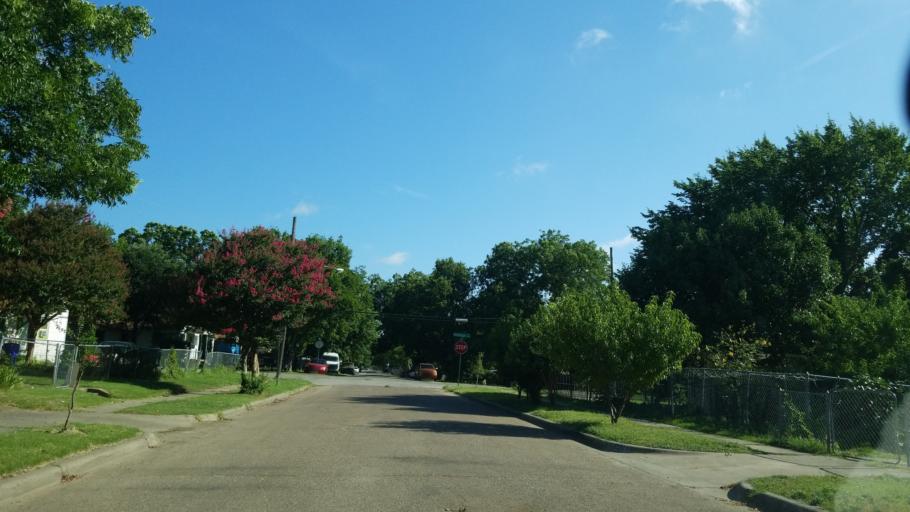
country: US
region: Texas
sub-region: Dallas County
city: Dallas
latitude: 32.7144
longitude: -96.8098
